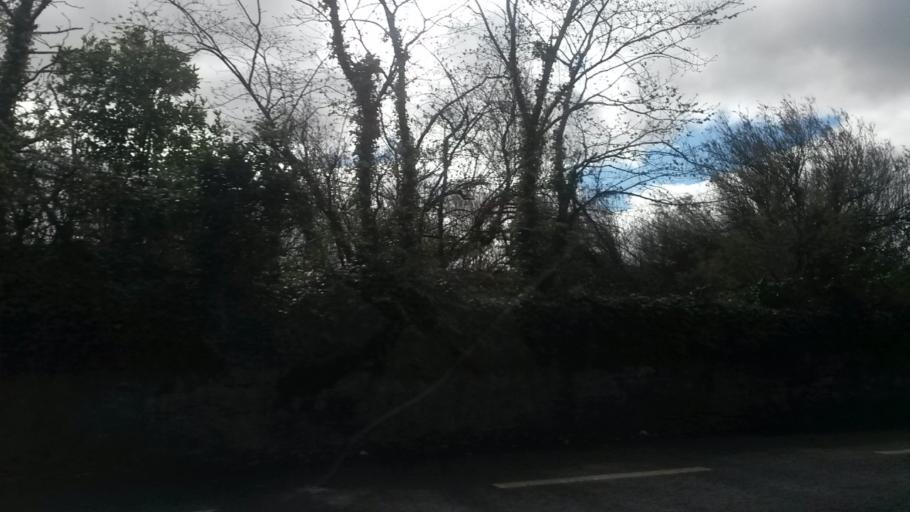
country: IE
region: Munster
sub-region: County Cork
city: Cobh
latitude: 51.8895
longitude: -8.3037
